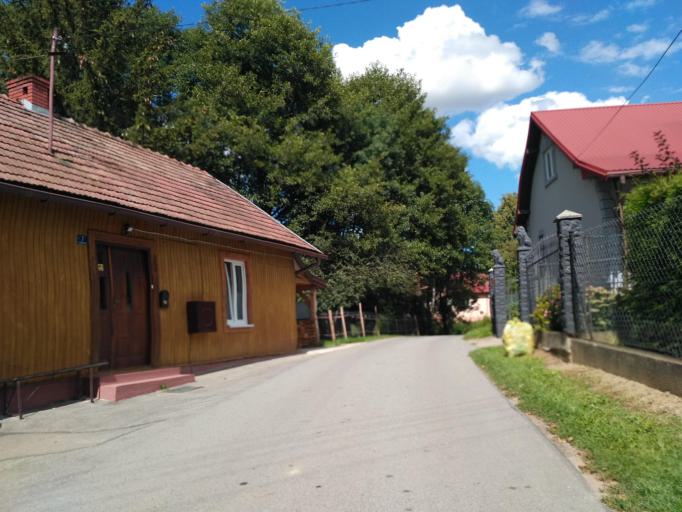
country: PL
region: Subcarpathian Voivodeship
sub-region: Powiat jasielski
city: Jaslo
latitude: 49.7600
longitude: 21.5028
